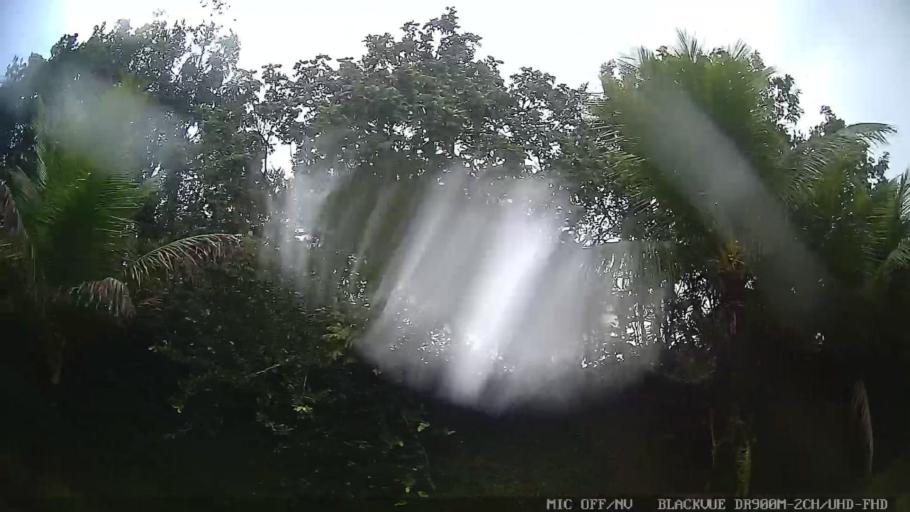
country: BR
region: Sao Paulo
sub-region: Peruibe
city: Peruibe
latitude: -24.2183
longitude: -46.9246
